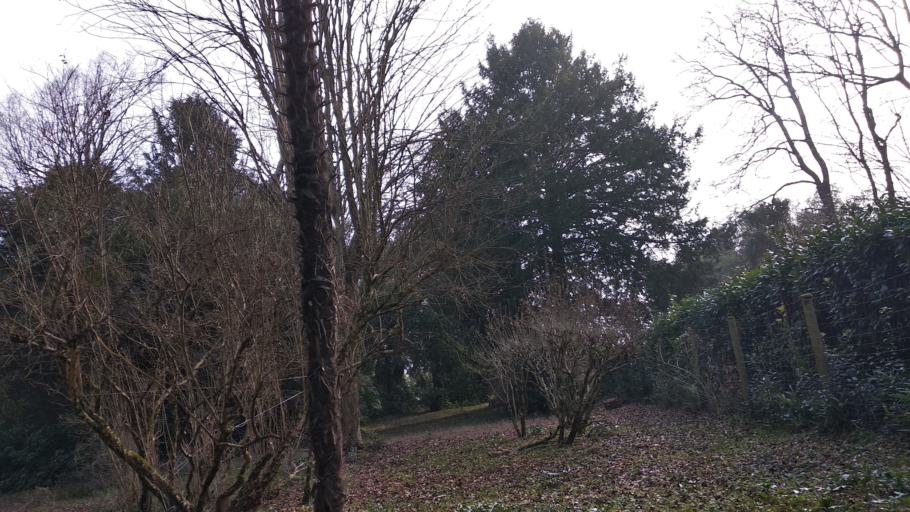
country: IT
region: Friuli Venezia Giulia
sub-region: Provincia di Udine
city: Villa Vicentina
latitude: 45.8217
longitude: 13.3686
